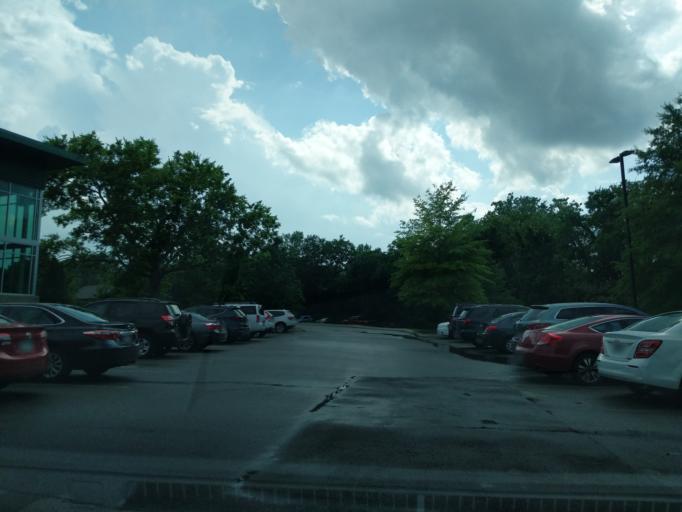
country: US
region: Tennessee
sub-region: Davidson County
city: Belle Meade
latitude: 36.0427
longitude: -86.9546
